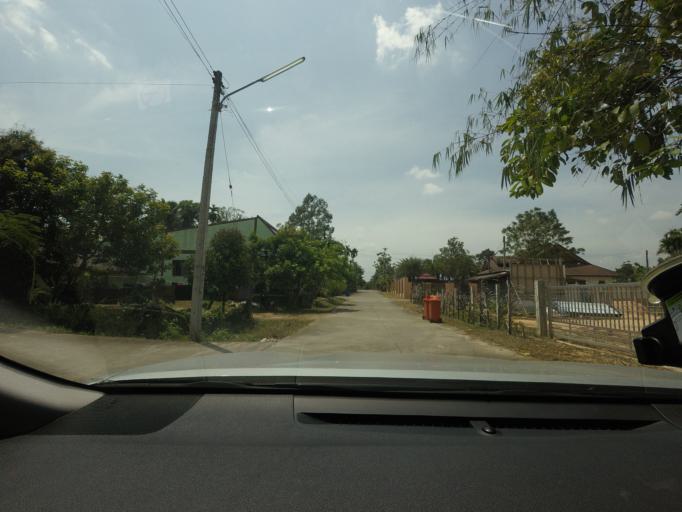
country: TH
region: Narathiwat
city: Rueso
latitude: 6.3817
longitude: 101.5092
